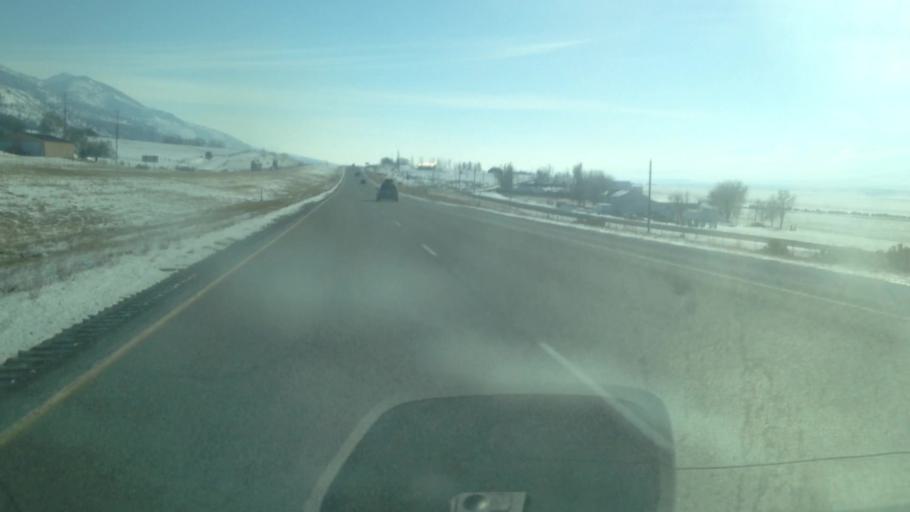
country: US
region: Idaho
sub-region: Oneida County
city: Malad City
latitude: 42.0318
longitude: -112.2097
